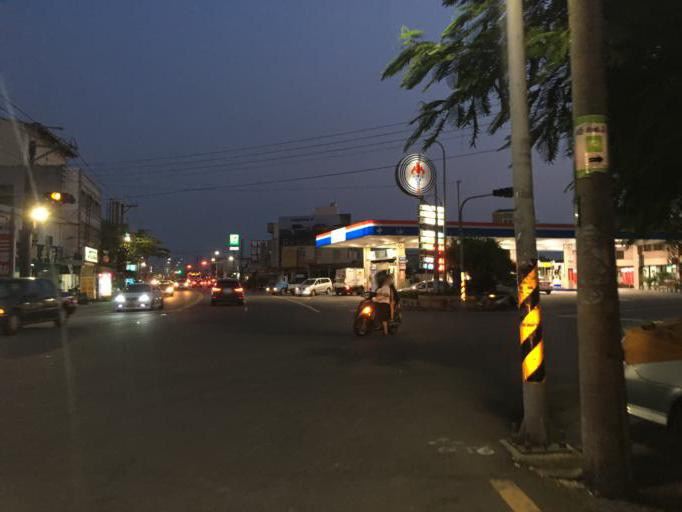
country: TW
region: Taiwan
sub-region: Chiayi
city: Taibao
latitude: 23.5514
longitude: 120.3473
